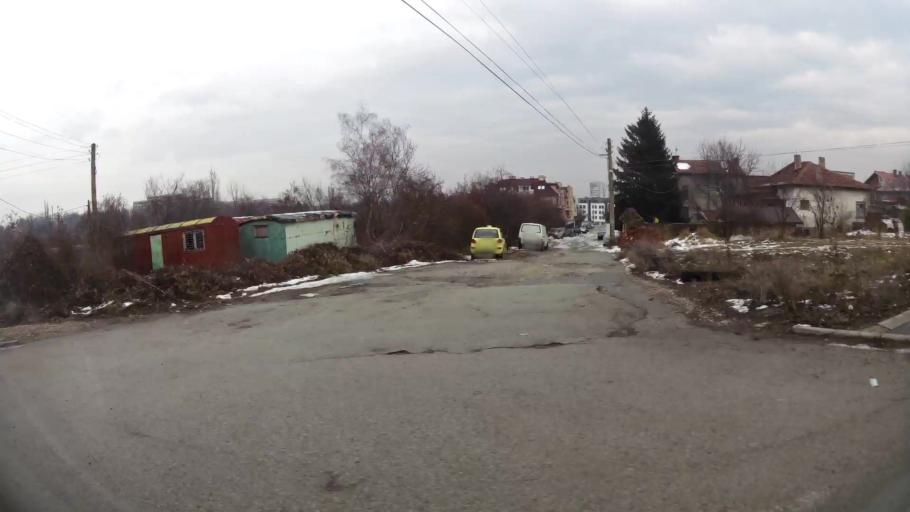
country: BG
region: Sofia-Capital
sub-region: Stolichna Obshtina
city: Sofia
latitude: 42.6699
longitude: 23.2446
